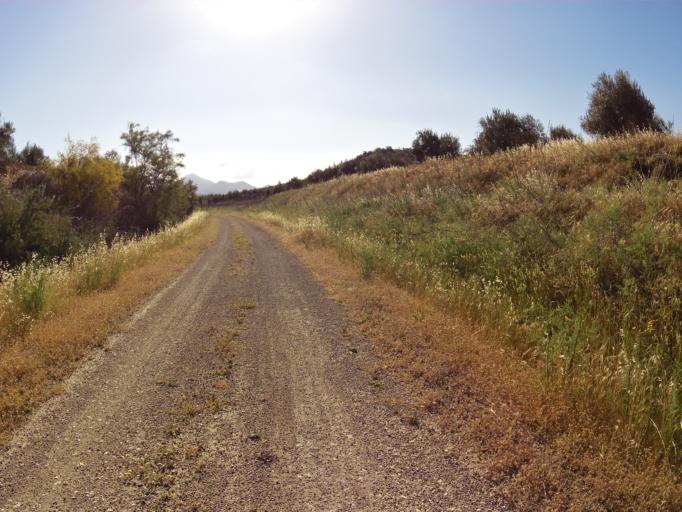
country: ES
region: Andalusia
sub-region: Province of Cordoba
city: Fuente-Tojar
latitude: 37.5819
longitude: -4.1954
